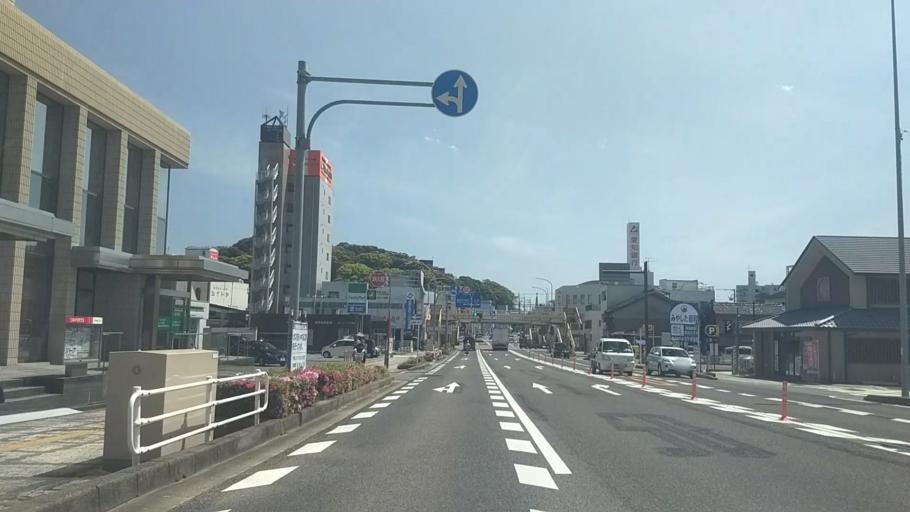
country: JP
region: Aichi
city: Okazaki
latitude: 34.9542
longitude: 137.1641
